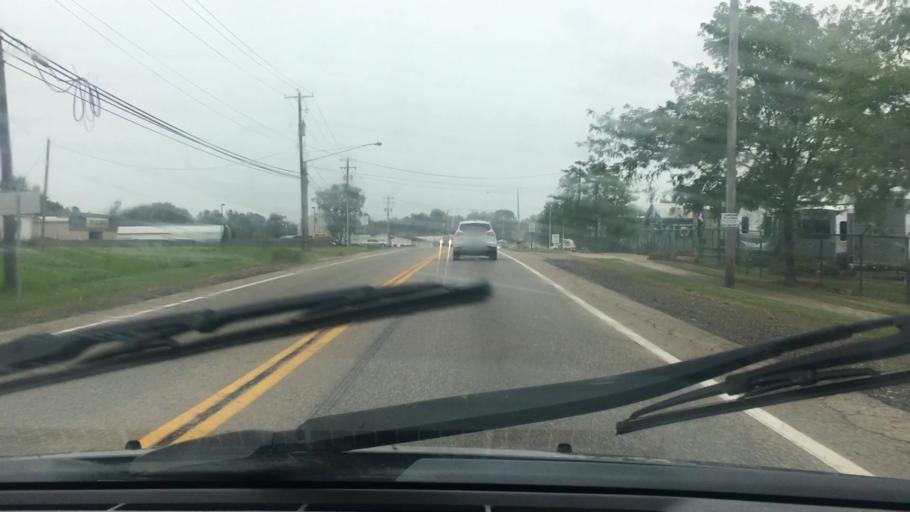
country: US
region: Ohio
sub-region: Portage County
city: Streetsboro
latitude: 41.2363
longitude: -81.3345
